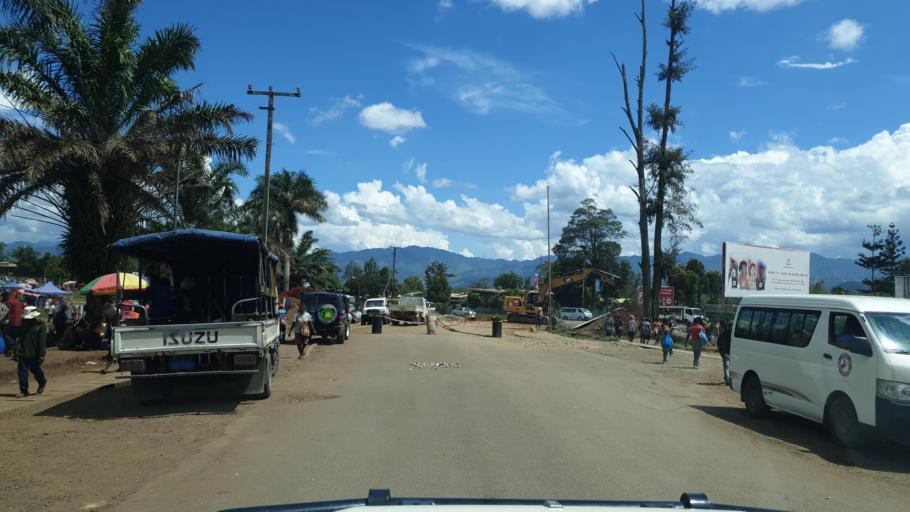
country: PG
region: Eastern Highlands
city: Goroka
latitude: -6.0743
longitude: 145.3897
